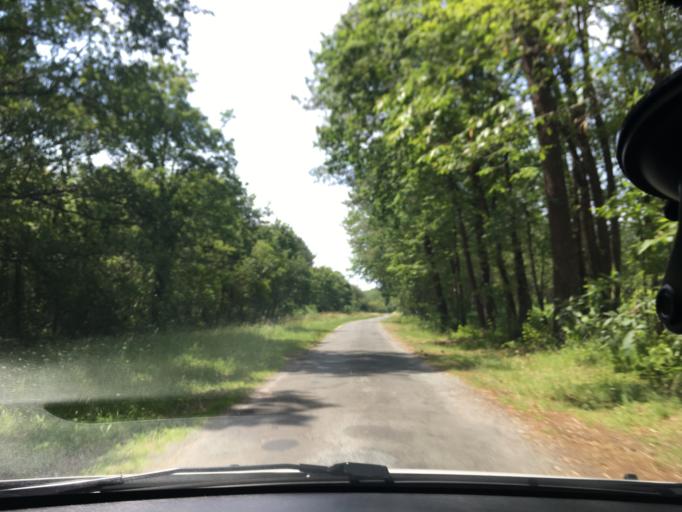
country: FR
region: Aquitaine
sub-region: Departement de la Gironde
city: Lesparre-Medoc
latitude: 45.2849
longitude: -0.9001
